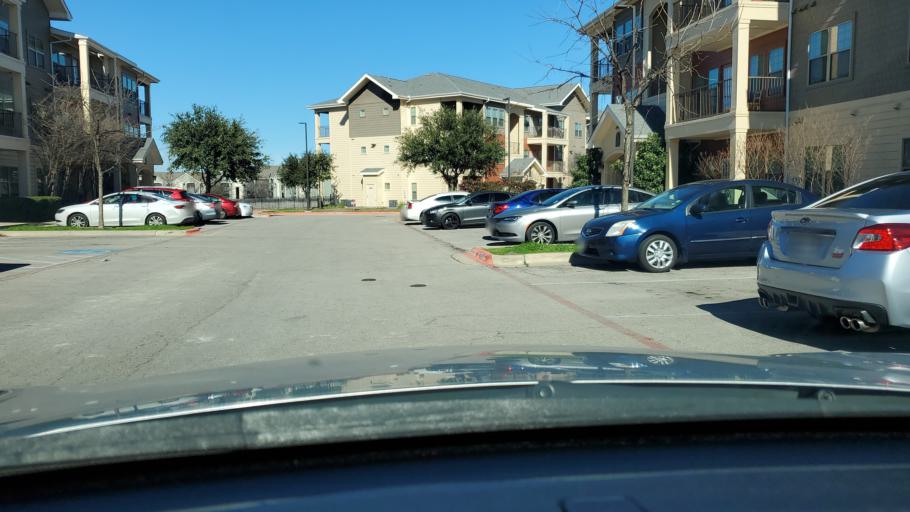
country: US
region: Texas
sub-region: Bell County
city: Killeen
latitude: 31.0845
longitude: -97.7332
